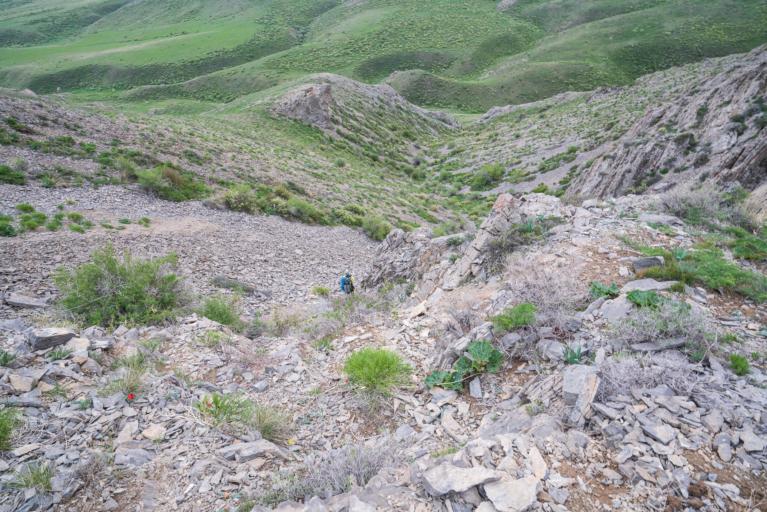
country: KZ
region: Ongtustik Qazaqstan
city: Ashchysay
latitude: 43.7560
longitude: 68.8113
